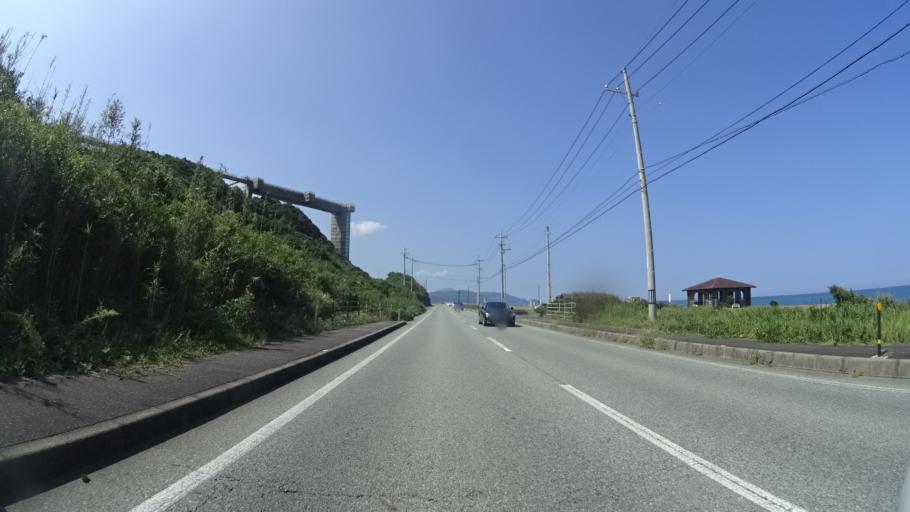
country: JP
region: Shimane
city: Masuda
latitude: 34.6817
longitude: 131.7725
